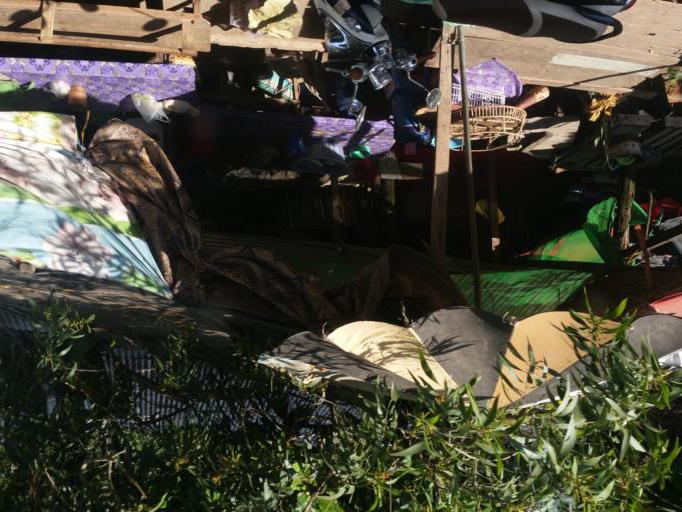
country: TH
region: Changwat Ubon Ratchathani
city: Sirindhorn
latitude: 15.1302
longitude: 105.4703
